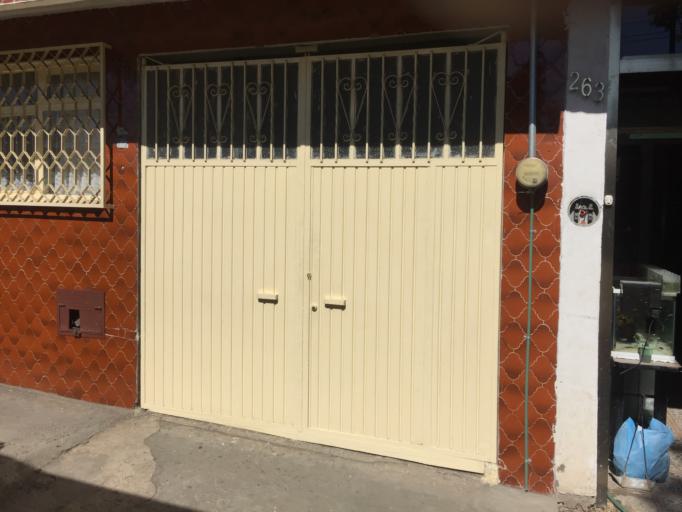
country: MX
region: Veracruz
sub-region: Xalapa
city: Xalapa de Enriquez
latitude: 19.5372
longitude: -96.9148
